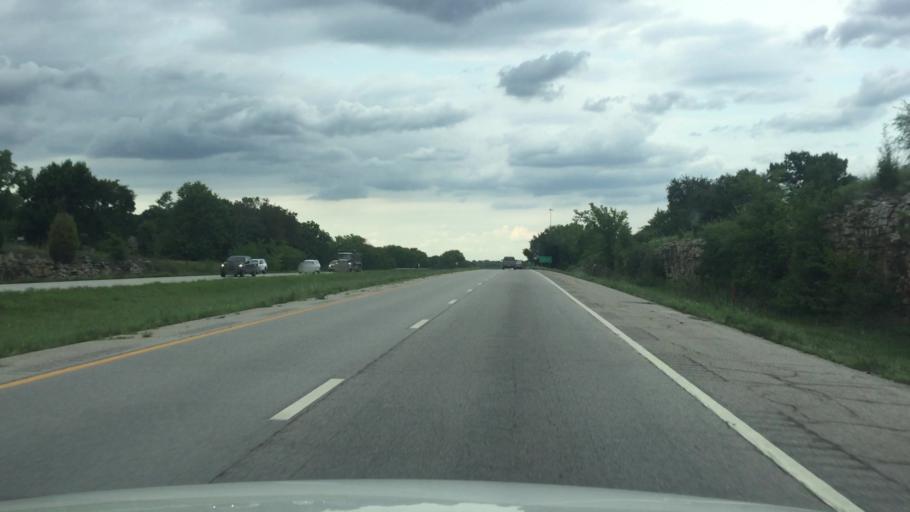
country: US
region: Missouri
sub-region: Cass County
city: Belton
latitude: 38.7971
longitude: -94.6759
